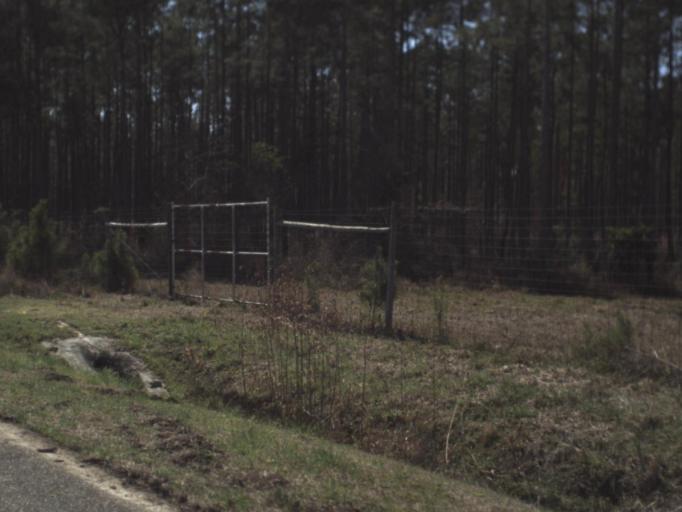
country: US
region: Florida
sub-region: Jackson County
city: Sneads
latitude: 30.6060
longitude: -85.0300
